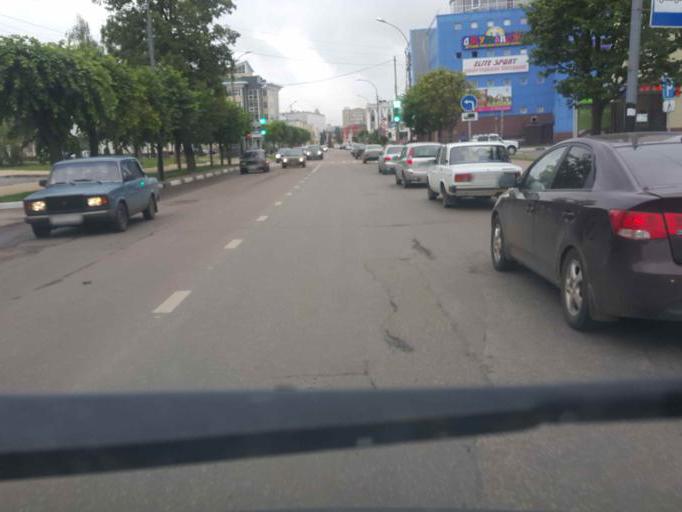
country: RU
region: Tambov
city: Tambov
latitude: 52.7183
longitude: 41.4535
